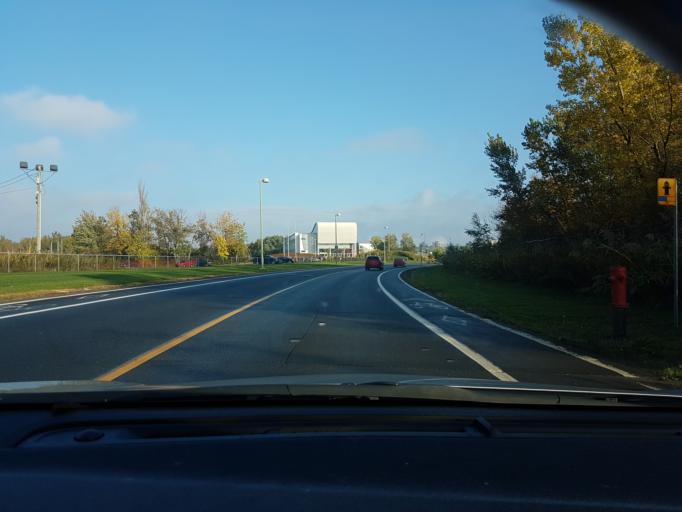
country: CA
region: Quebec
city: L'Ancienne-Lorette
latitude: 46.7978
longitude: -71.2968
